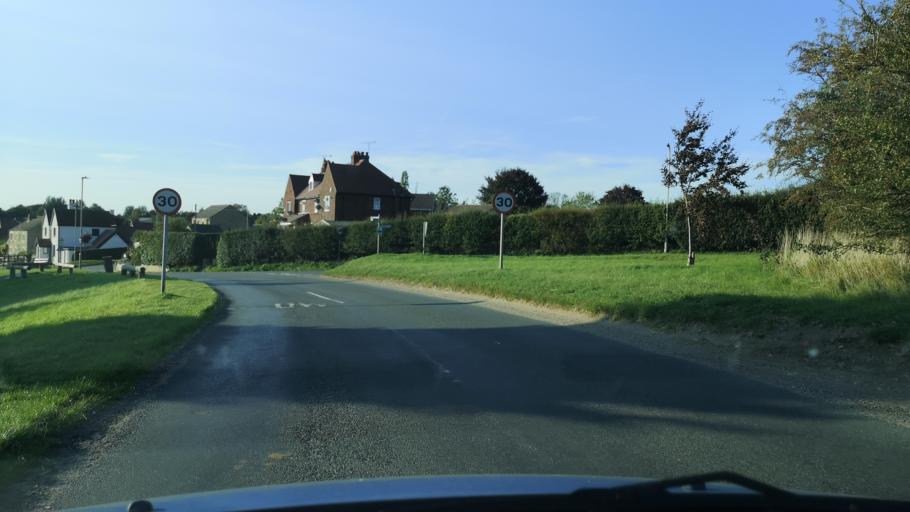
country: GB
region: England
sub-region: Doncaster
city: Norton
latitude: 53.6435
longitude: -1.2025
